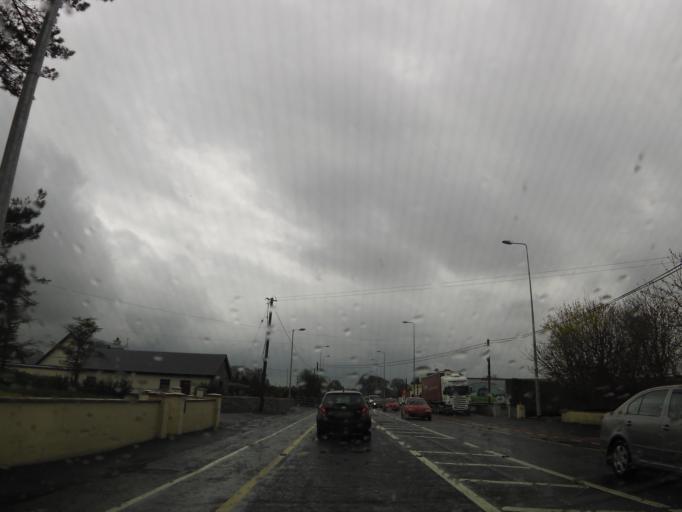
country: IE
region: Connaught
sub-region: County Galway
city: Claregalway
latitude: 53.3908
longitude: -8.9146
